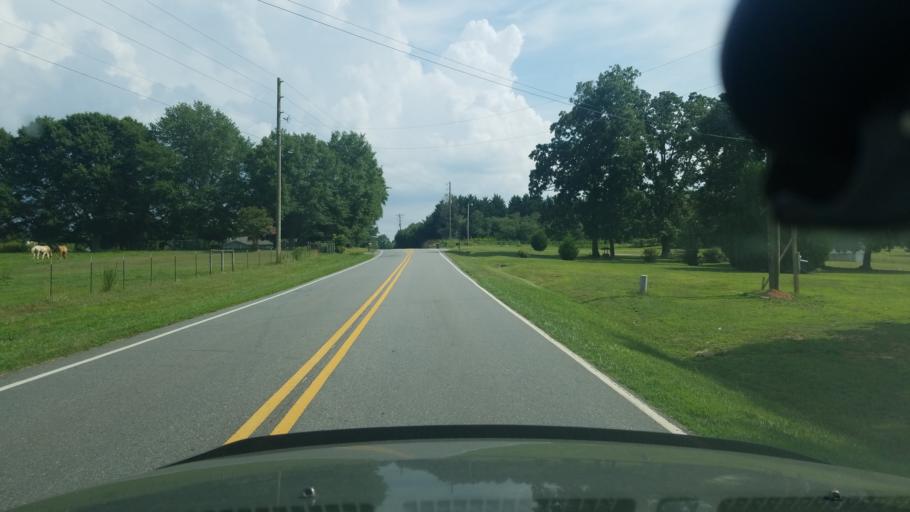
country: US
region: Georgia
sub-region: Hall County
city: Flowery Branch
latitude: 34.2795
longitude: -84.0009
